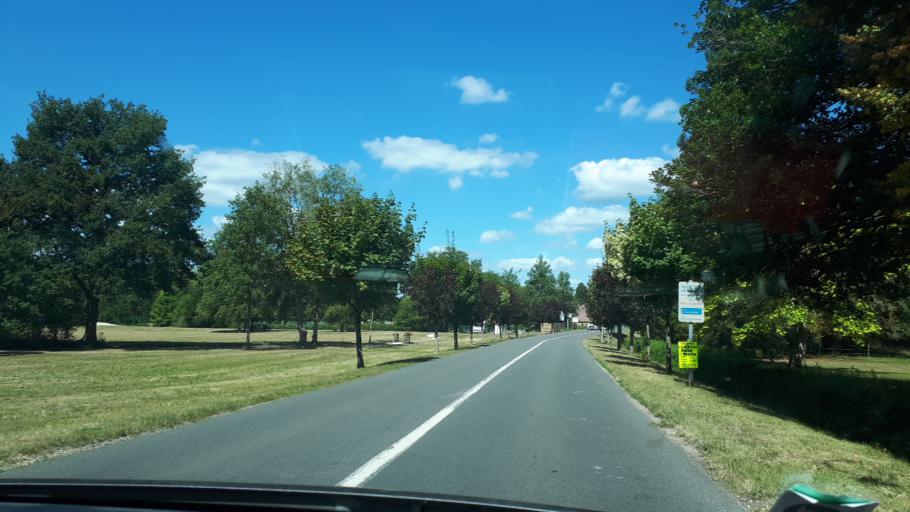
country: FR
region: Centre
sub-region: Departement du Loir-et-Cher
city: Neung-sur-Beuvron
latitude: 47.5317
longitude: 1.8079
